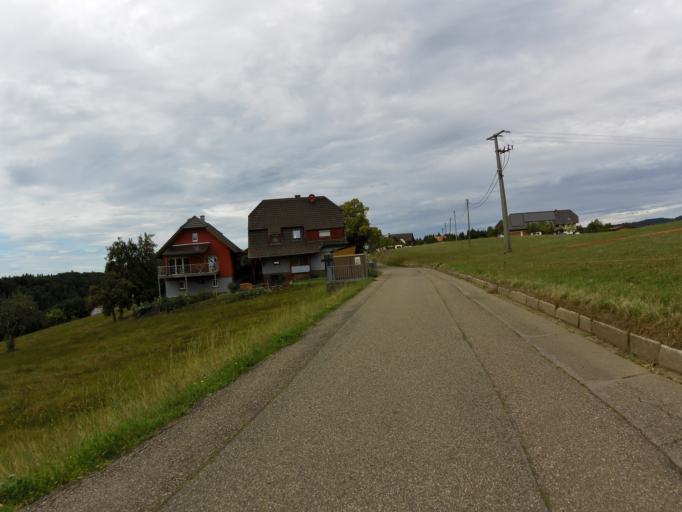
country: DE
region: Baden-Wuerttemberg
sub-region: Freiburg Region
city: Hohberg
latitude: 48.3208
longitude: 7.8990
